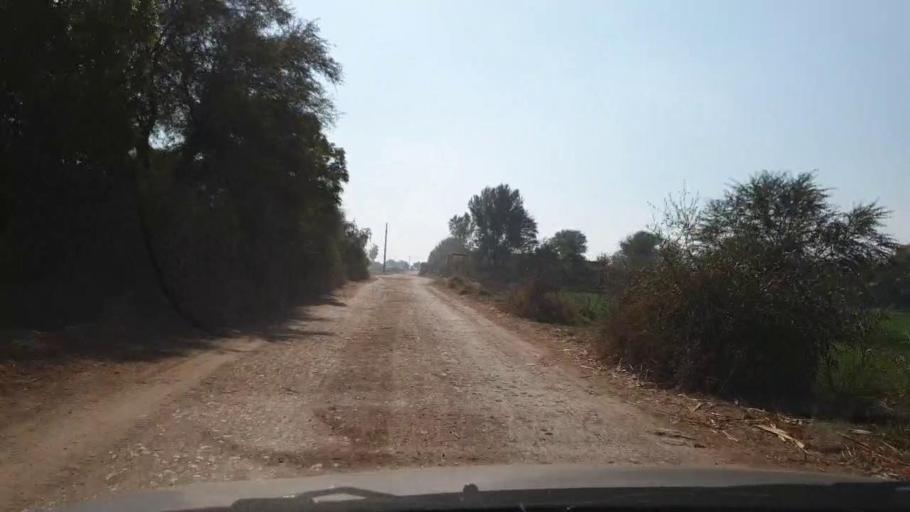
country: PK
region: Sindh
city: Jhol
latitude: 25.9388
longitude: 68.7999
